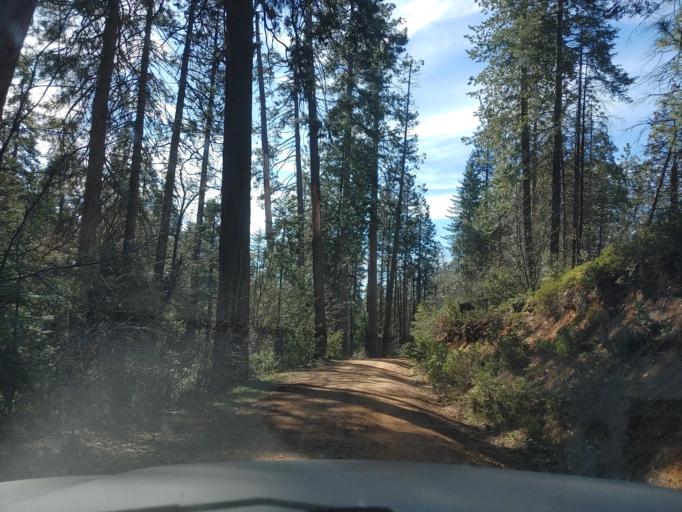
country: US
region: California
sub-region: Madera County
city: Ahwahnee
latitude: 37.4223
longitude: -119.6773
